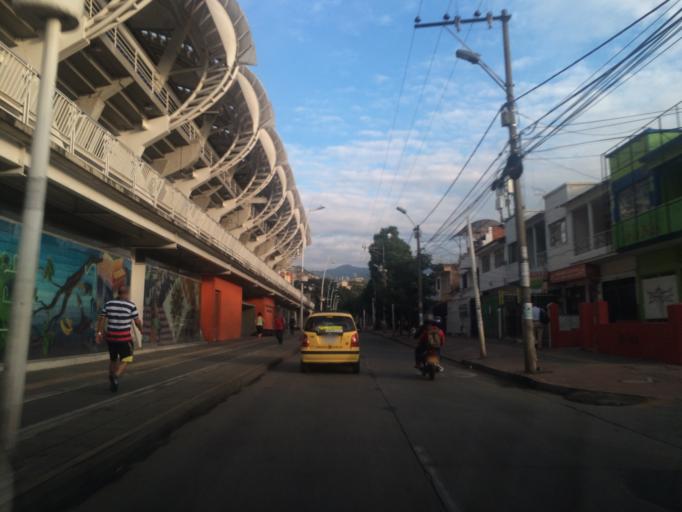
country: CO
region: Valle del Cauca
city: Cali
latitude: 3.4298
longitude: -76.5401
